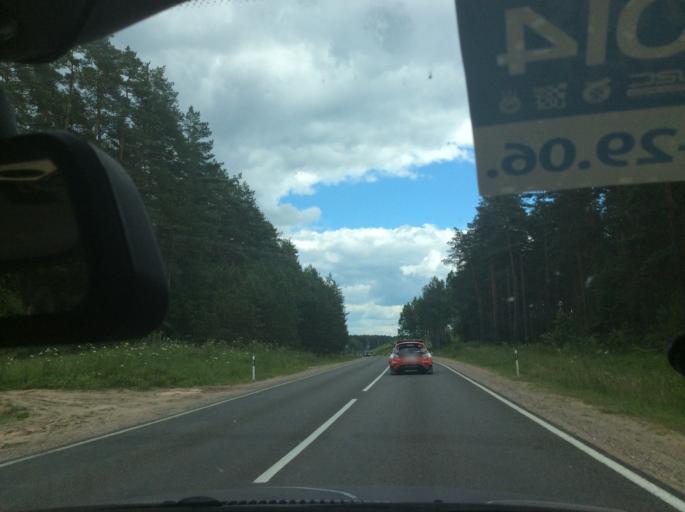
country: LT
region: Alytaus apskritis
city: Druskininkai
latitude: 54.0351
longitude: 23.9562
